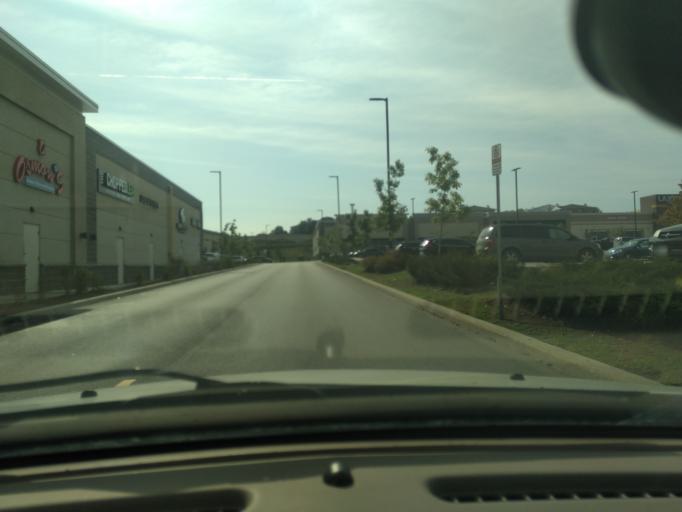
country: CA
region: Ontario
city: Barrie
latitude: 44.4150
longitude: -79.6784
